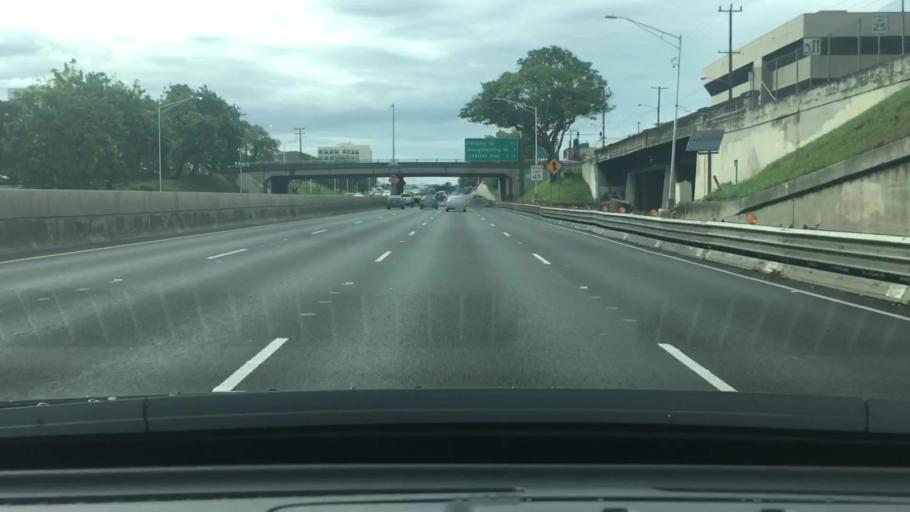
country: US
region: Hawaii
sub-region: Honolulu County
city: Honolulu
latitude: 21.3179
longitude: -157.8572
